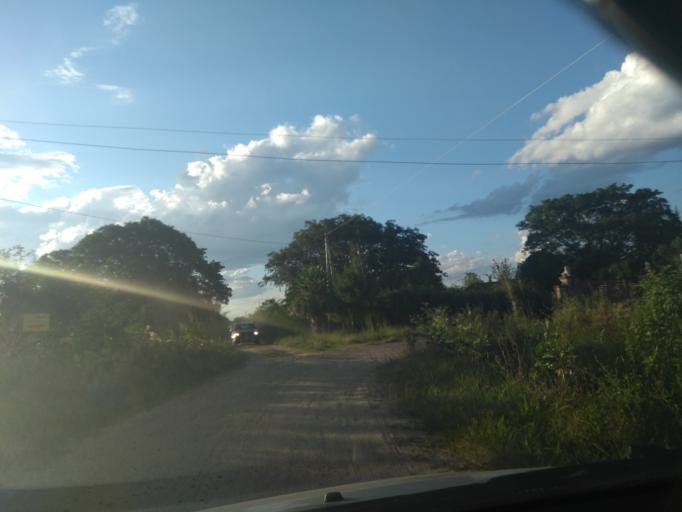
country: AR
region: Chaco
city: Colonia Benitez
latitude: -27.3913
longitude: -58.9410
